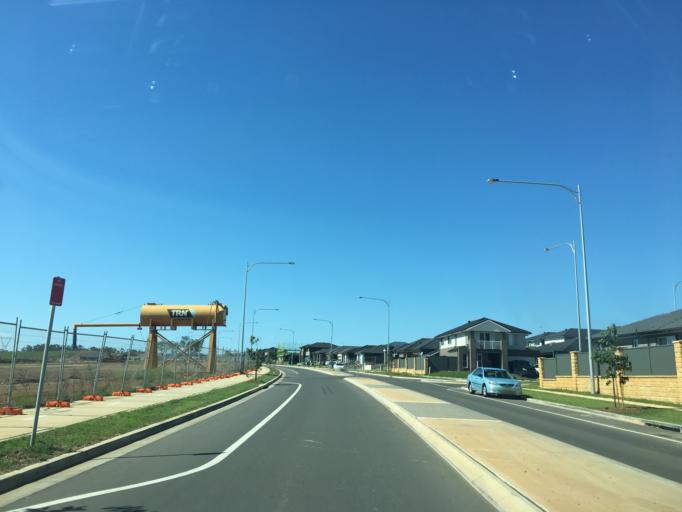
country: AU
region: New South Wales
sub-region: Campbelltown Municipality
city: Denham Court
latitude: -33.9956
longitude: 150.7940
